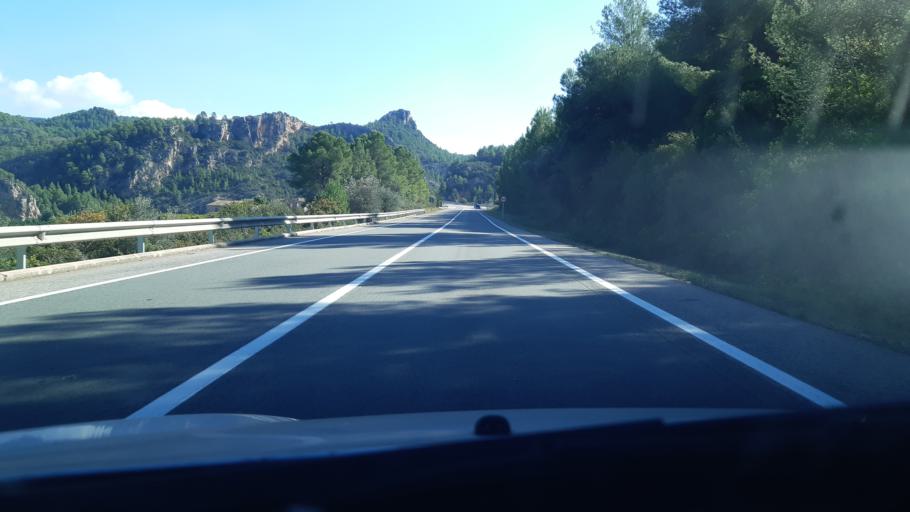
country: ES
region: Catalonia
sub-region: Provincia de Tarragona
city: Benifallet
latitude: 40.9449
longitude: 0.4843
